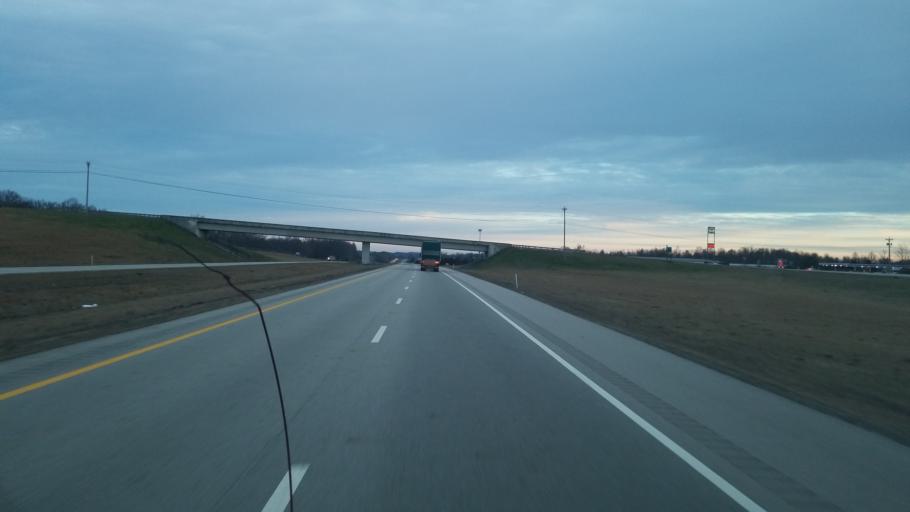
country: US
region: Tennessee
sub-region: Putnam County
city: Cookeville
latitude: 36.0539
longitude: -85.5074
